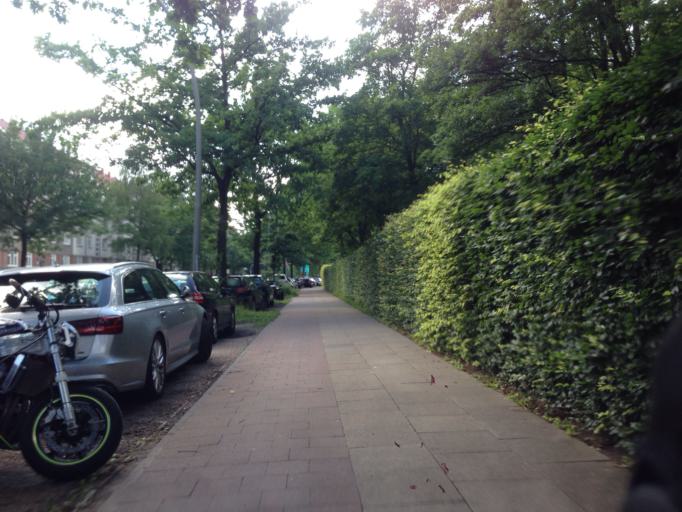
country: DE
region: Hamburg
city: Winterhude
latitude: 53.5909
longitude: 10.0096
